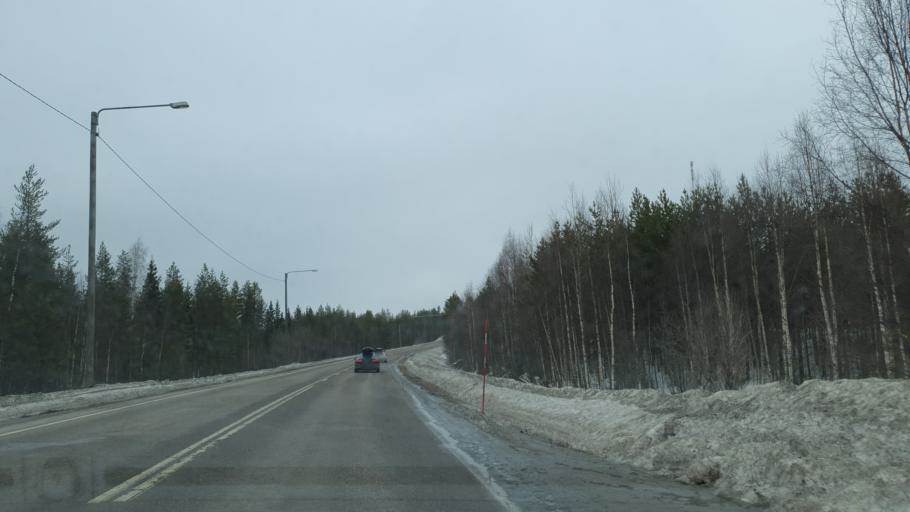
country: FI
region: Lapland
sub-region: Torniolaakso
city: Pello
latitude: 66.8328
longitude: 24.0026
